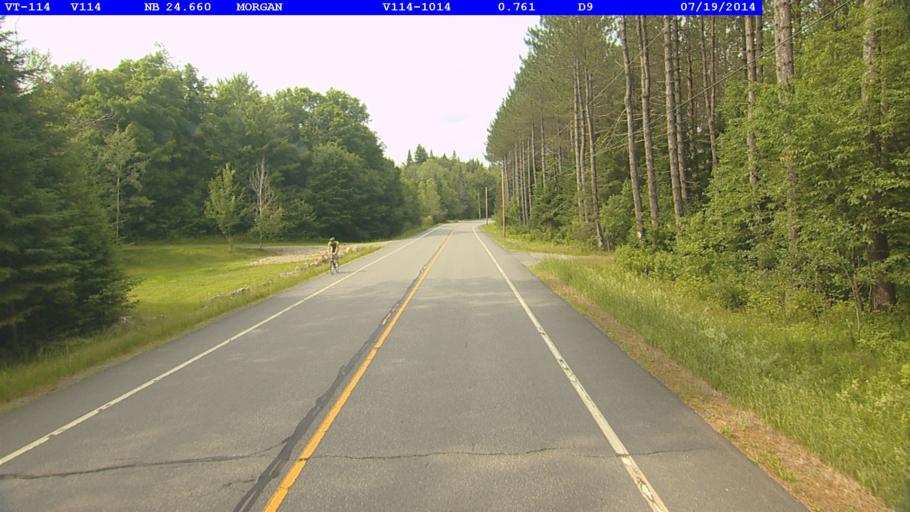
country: CA
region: Quebec
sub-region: Estrie
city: Coaticook
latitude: 44.8575
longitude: -71.9092
